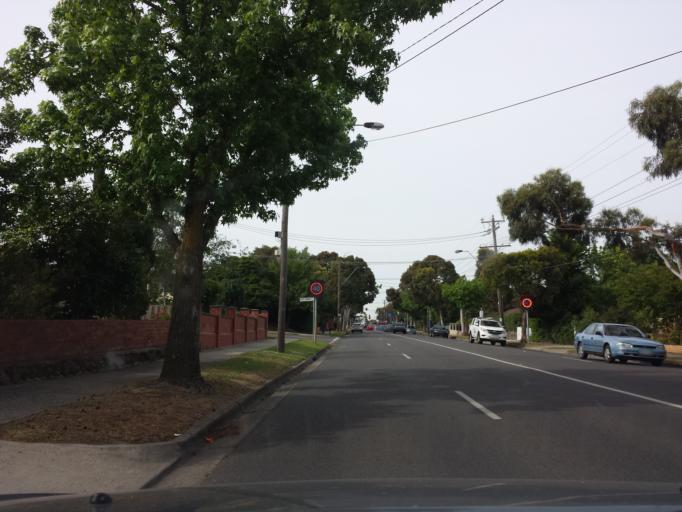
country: AU
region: Victoria
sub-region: Monash
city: Ashwood
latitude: -37.8726
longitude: 145.1296
